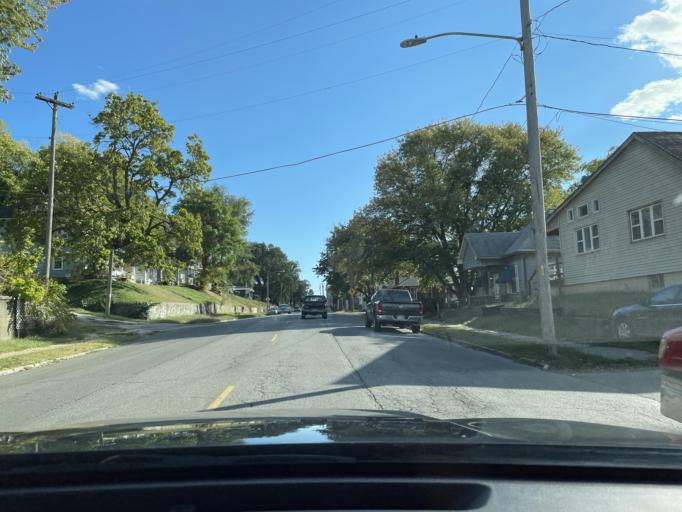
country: US
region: Kansas
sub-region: Doniphan County
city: Elwood
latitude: 39.7182
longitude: -94.8623
